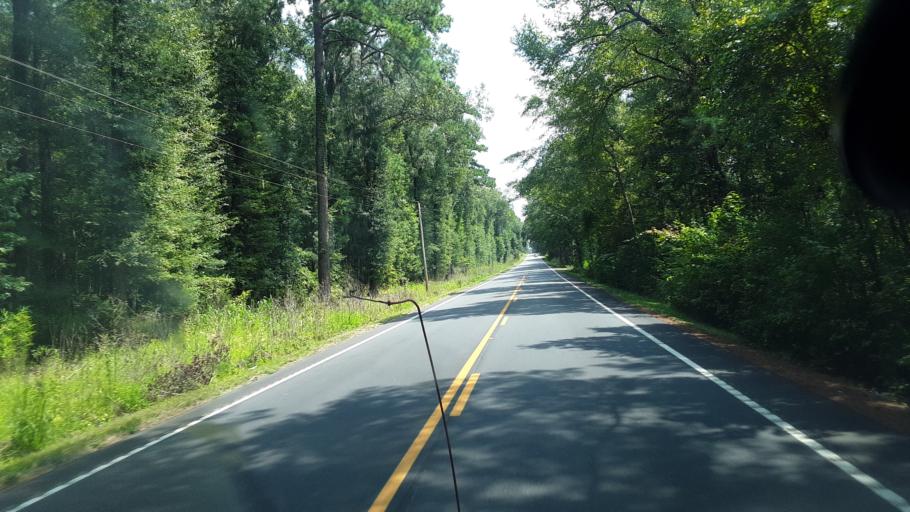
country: US
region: South Carolina
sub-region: Jasper County
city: Ridgeland
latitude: 32.5365
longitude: -80.9082
